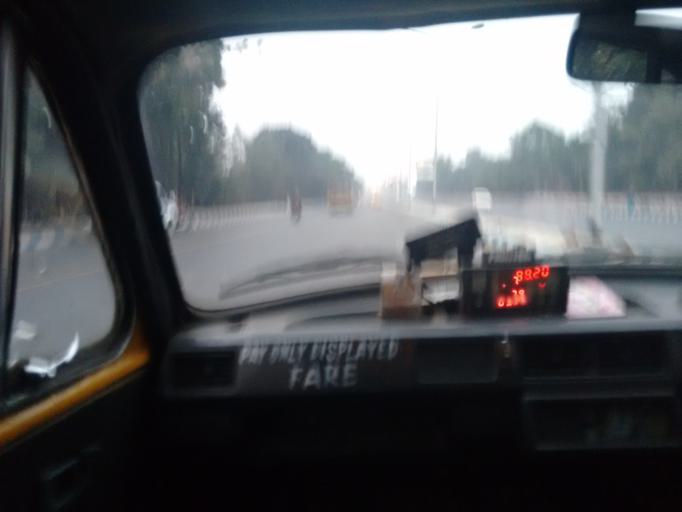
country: IN
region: West Bengal
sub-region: Kolkata
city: Kolkata
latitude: 22.5649
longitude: 88.4070
